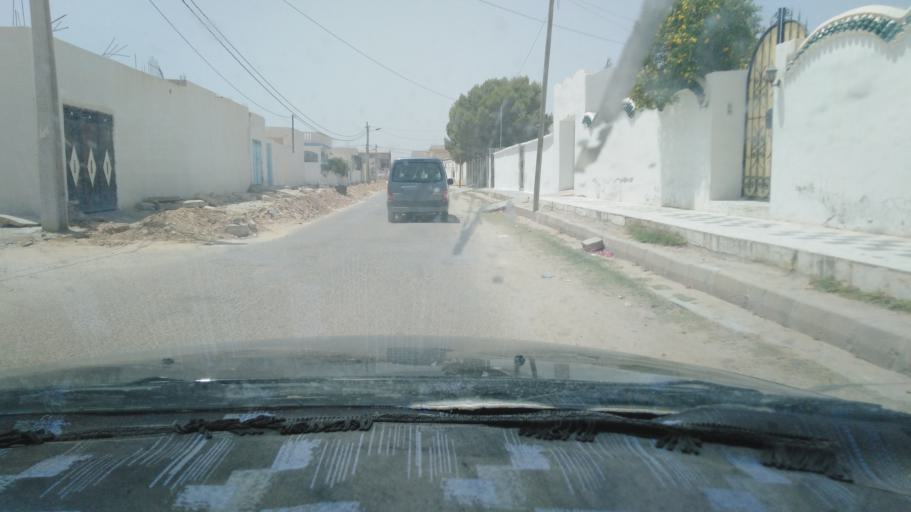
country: TN
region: Qabis
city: Matmata
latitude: 33.6179
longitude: 10.2788
